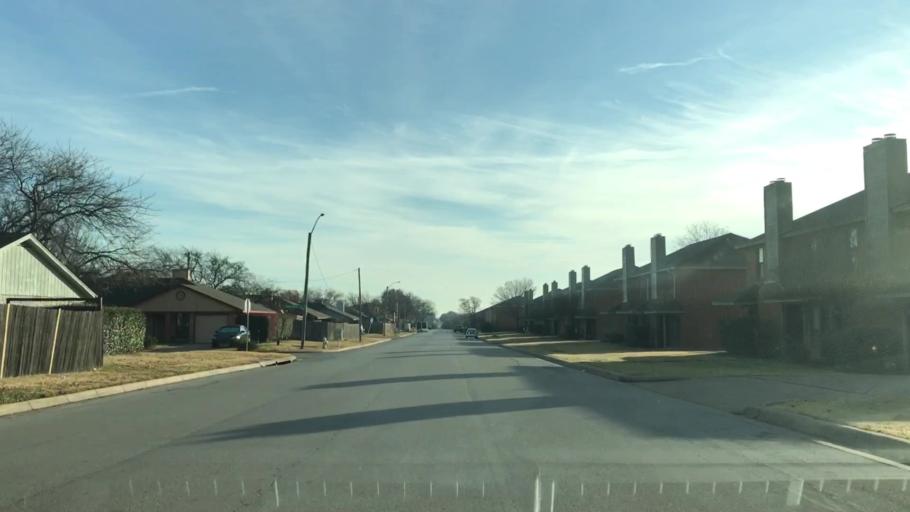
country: US
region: Texas
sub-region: Tarrant County
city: Sansom Park
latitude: 32.8220
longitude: -97.4173
